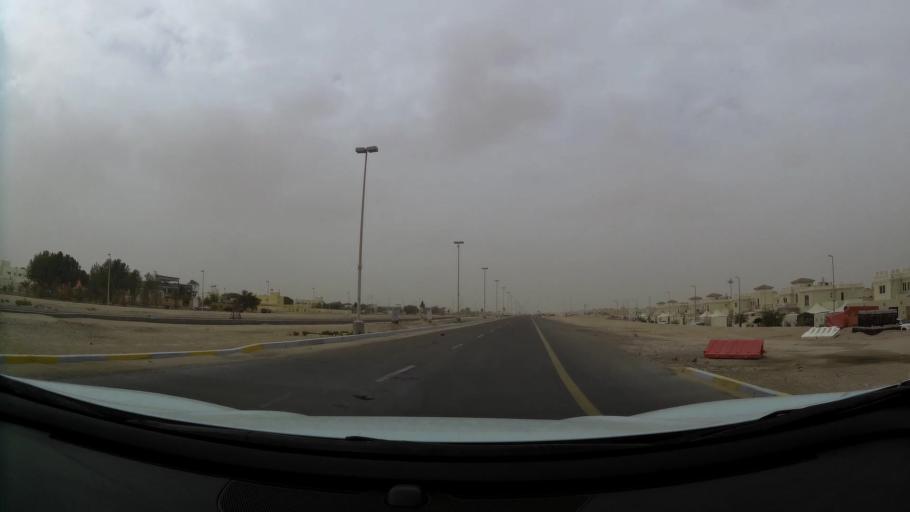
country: AE
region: Abu Dhabi
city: Abu Dhabi
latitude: 24.4301
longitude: 54.7448
